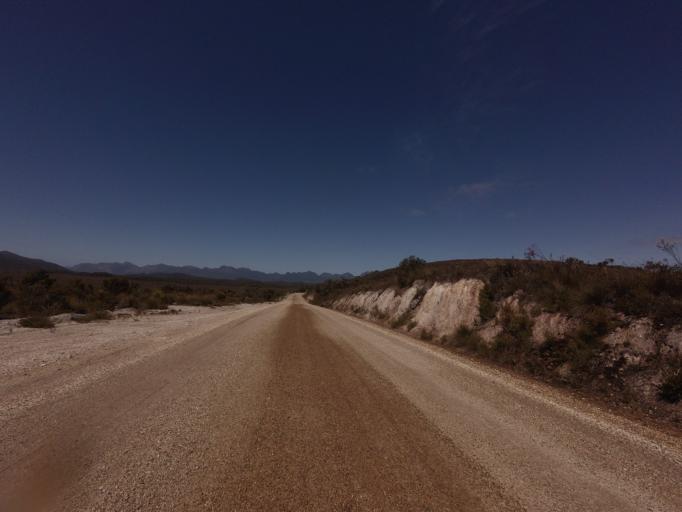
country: AU
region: Tasmania
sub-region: Huon Valley
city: Geeveston
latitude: -43.0340
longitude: 146.3338
